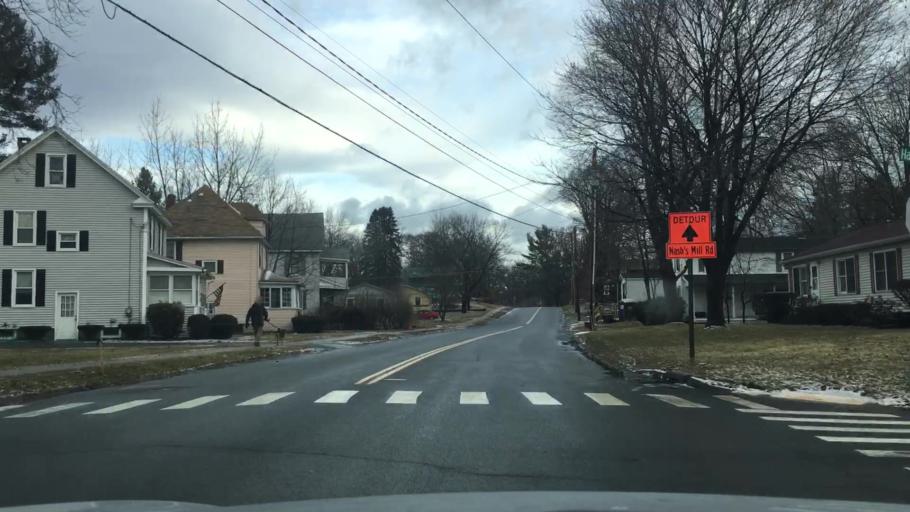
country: US
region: Massachusetts
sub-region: Franklin County
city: Greenfield
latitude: 42.5984
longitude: -72.6112
